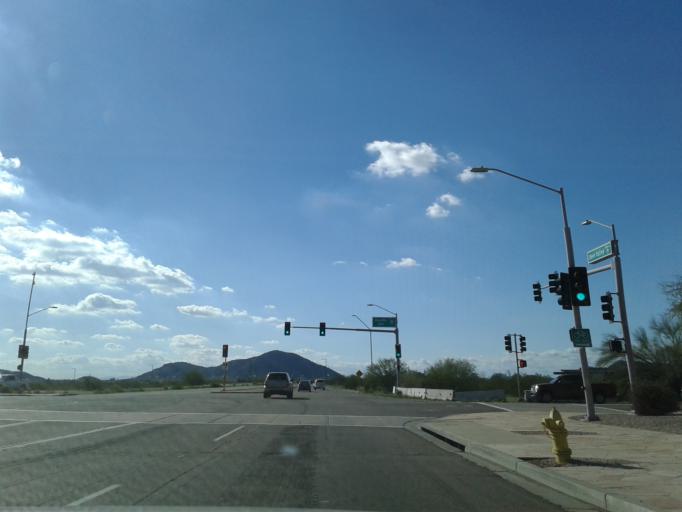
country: US
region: Arizona
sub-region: Maricopa County
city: Cave Creek
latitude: 33.6843
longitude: -112.0045
